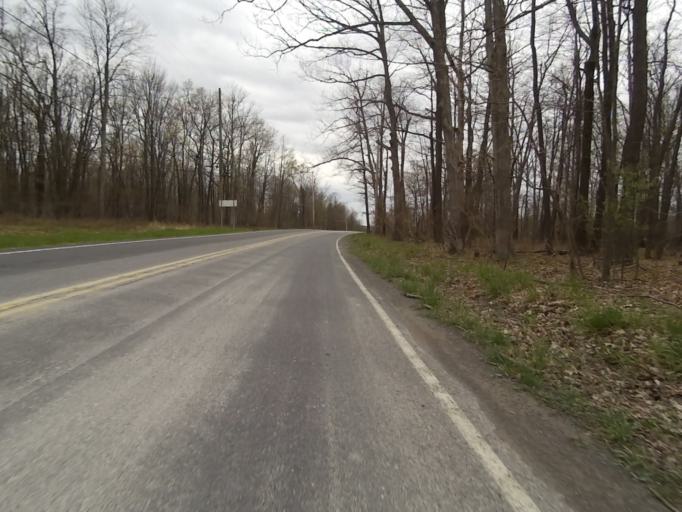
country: US
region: Pennsylvania
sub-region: Clearfield County
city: Troy
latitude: 40.9021
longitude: -78.1305
